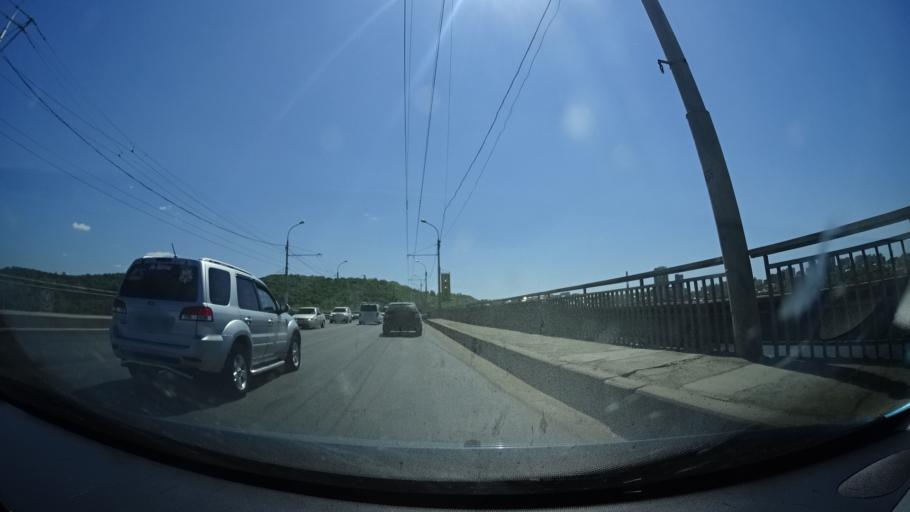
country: RU
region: Bashkortostan
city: Ufa
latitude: 54.7585
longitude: 55.9637
